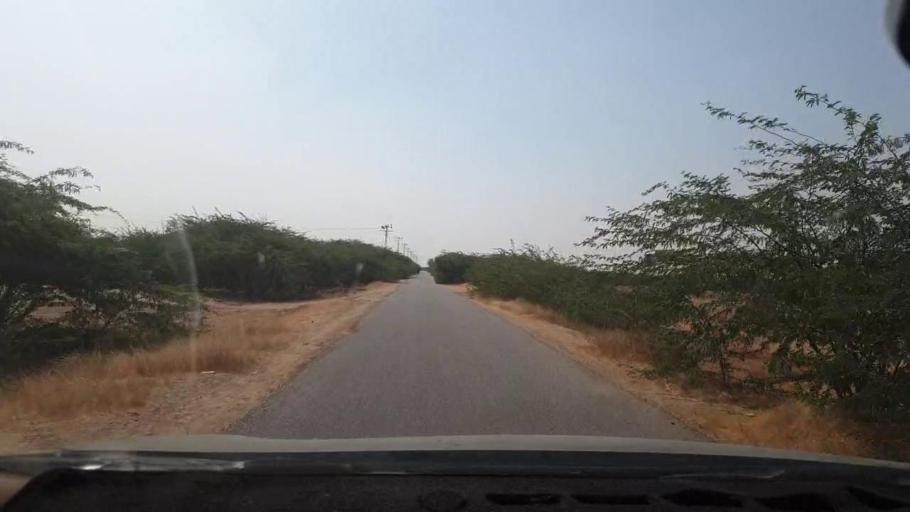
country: PK
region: Sindh
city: Malir Cantonment
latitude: 25.1161
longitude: 67.2112
